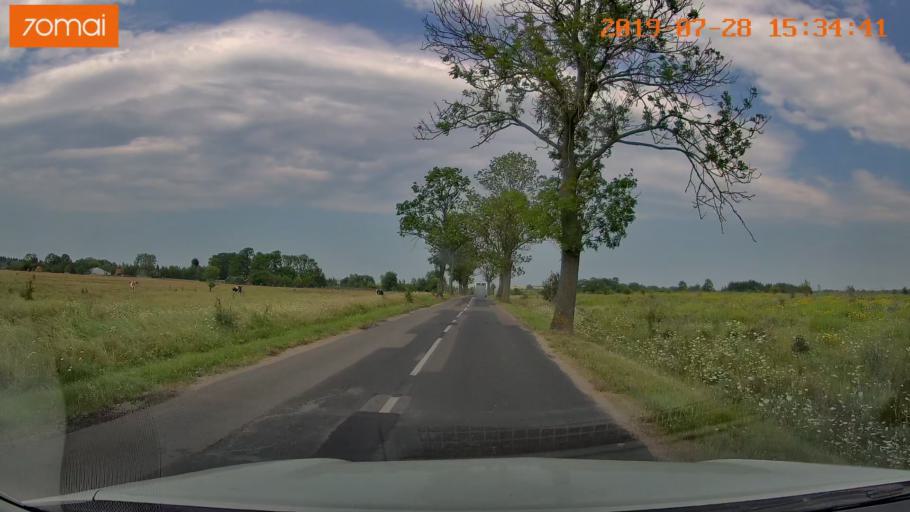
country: RU
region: Kaliningrad
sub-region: Gorod Kaliningrad
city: Yantarnyy
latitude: 54.8817
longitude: 19.9714
